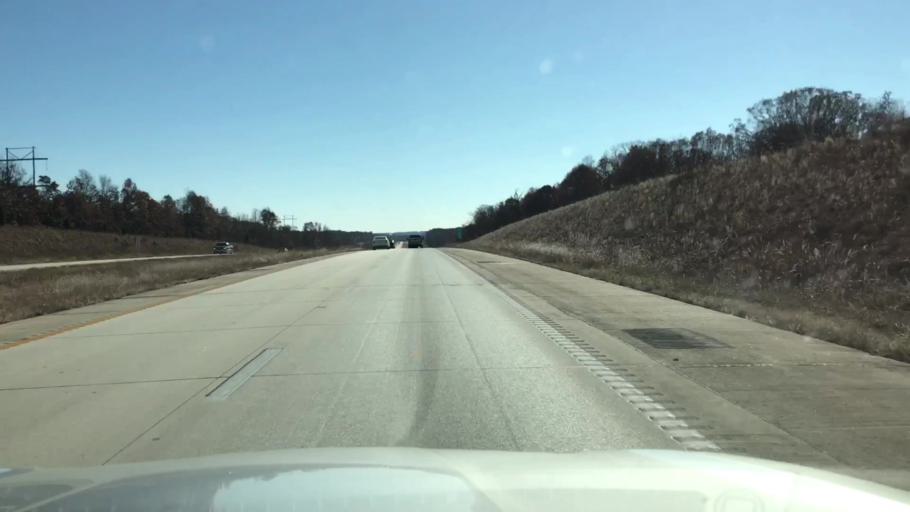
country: US
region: Missouri
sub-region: Jasper County
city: Duquesne
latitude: 37.0243
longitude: -94.4301
